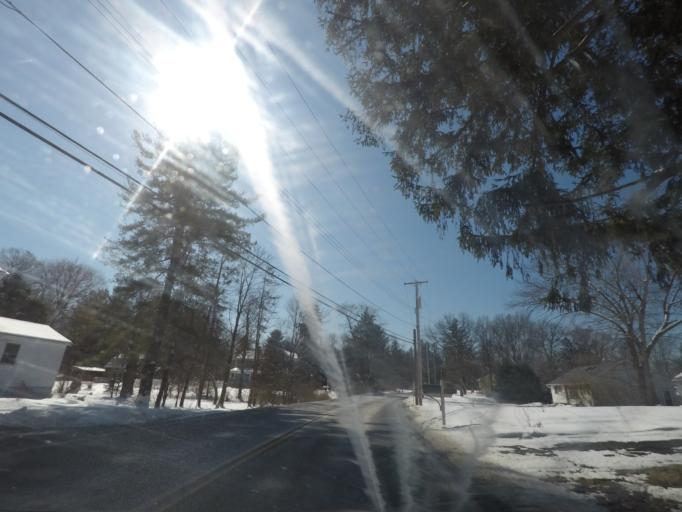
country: US
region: New York
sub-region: Schenectady County
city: Niskayuna
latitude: 42.7782
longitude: -73.8467
